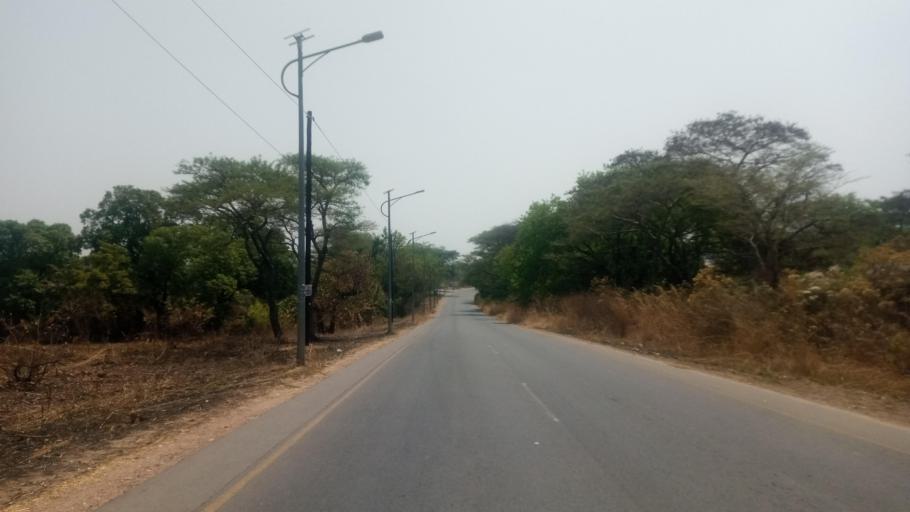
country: ZM
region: Lusaka
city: Lusaka
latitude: -15.4607
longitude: 28.4350
